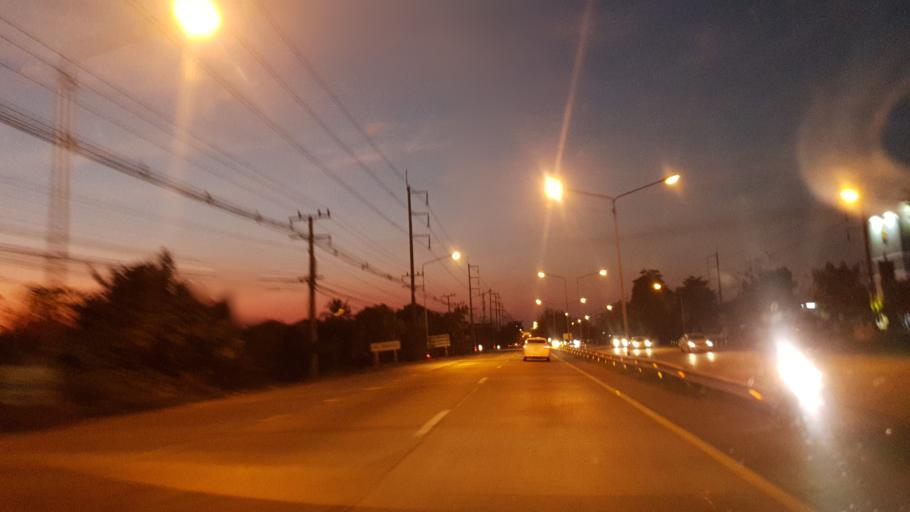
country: TH
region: Phitsanulok
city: Wang Thong
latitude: 16.8354
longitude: 100.4003
